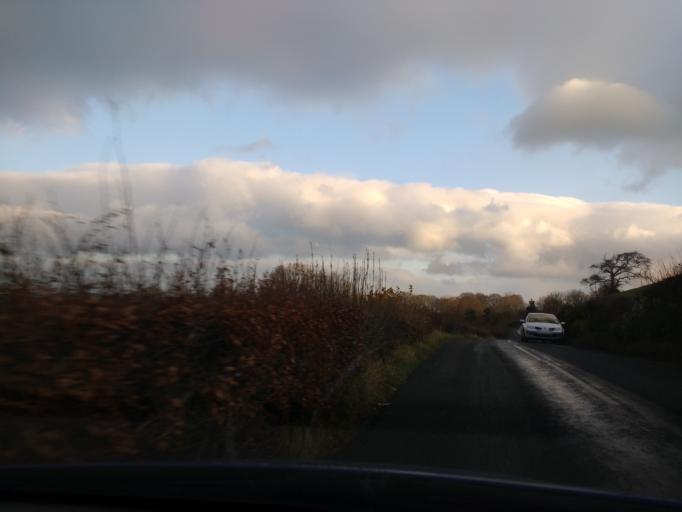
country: GB
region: England
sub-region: Lancashire
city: Caton
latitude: 54.0641
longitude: -2.7228
